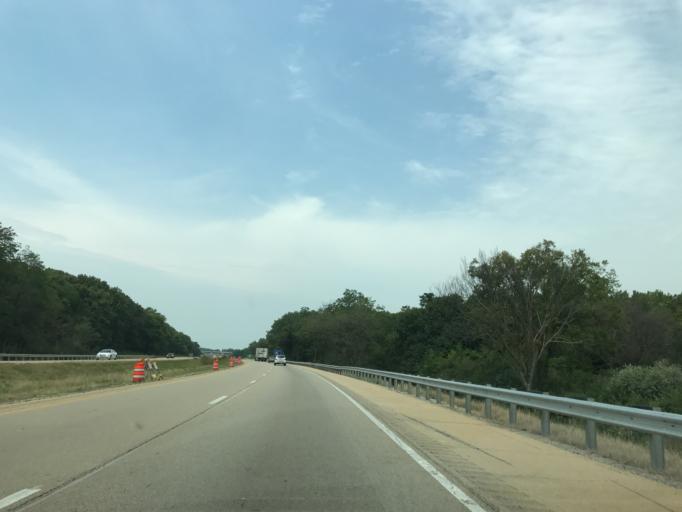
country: US
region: Illinois
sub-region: LaSalle County
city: La Salle
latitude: 41.3715
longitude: -89.0768
